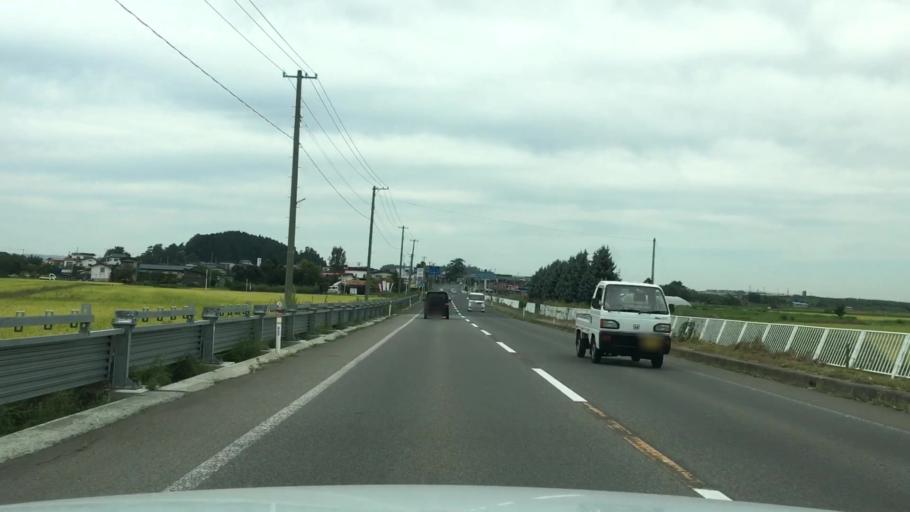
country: JP
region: Aomori
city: Hirosaki
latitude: 40.6383
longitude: 140.4474
